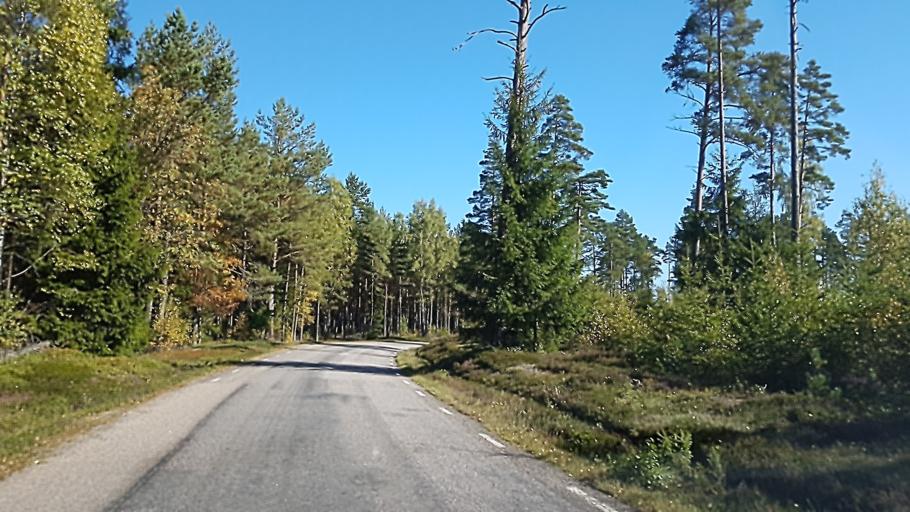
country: SE
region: Kronoberg
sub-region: Ljungby Kommun
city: Ljungby
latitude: 56.8176
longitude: 14.0408
